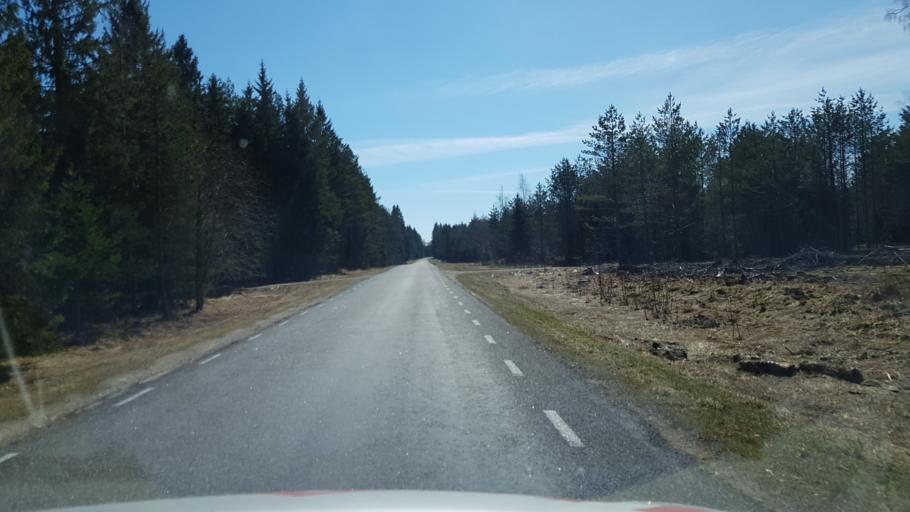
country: EE
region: Laeaene-Virumaa
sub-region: Vinni vald
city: Vinni
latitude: 59.1455
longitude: 26.5217
